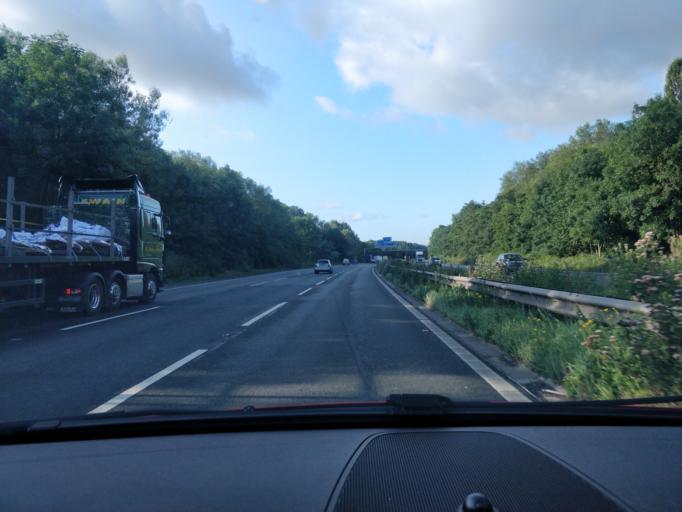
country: GB
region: England
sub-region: Knowsley
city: Prescot
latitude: 53.4171
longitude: -2.8131
